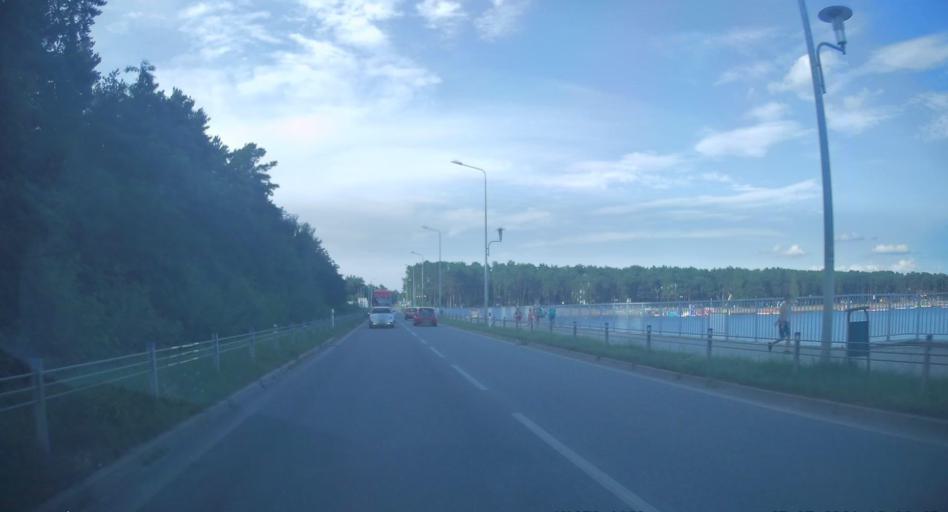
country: PL
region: Swietokrzyskie
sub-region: Powiat konecki
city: Smykow
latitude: 51.1162
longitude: 20.3505
